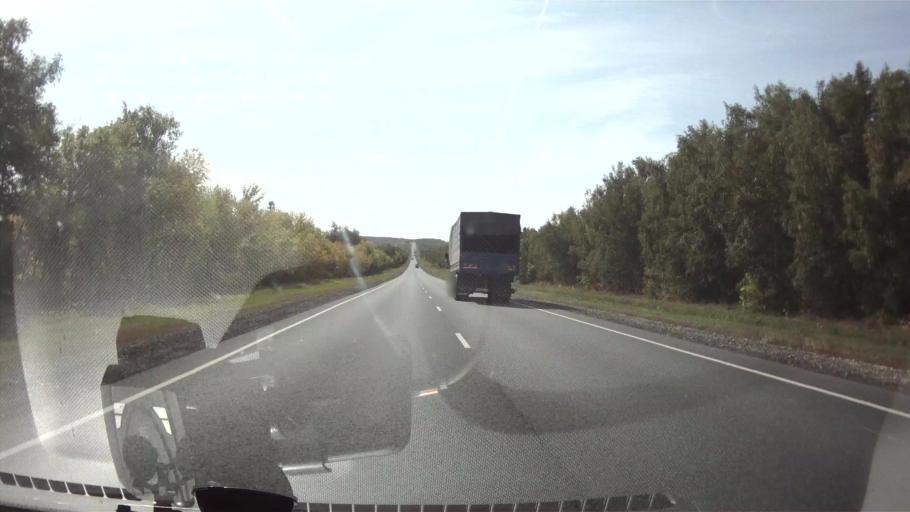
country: RU
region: Saratov
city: Khvalynsk
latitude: 52.5844
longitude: 48.1214
